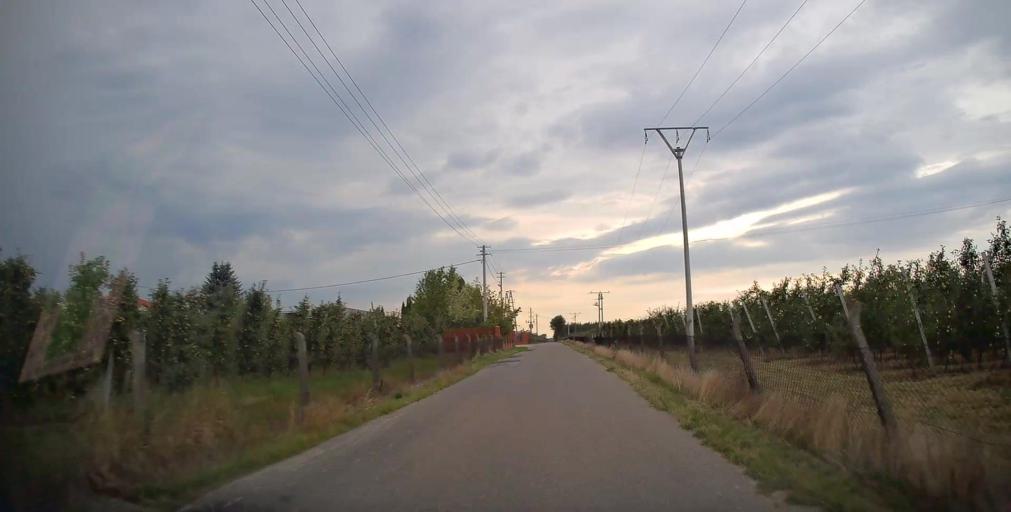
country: PL
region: Masovian Voivodeship
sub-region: Powiat grojecki
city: Jasieniec
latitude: 51.7909
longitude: 20.8974
